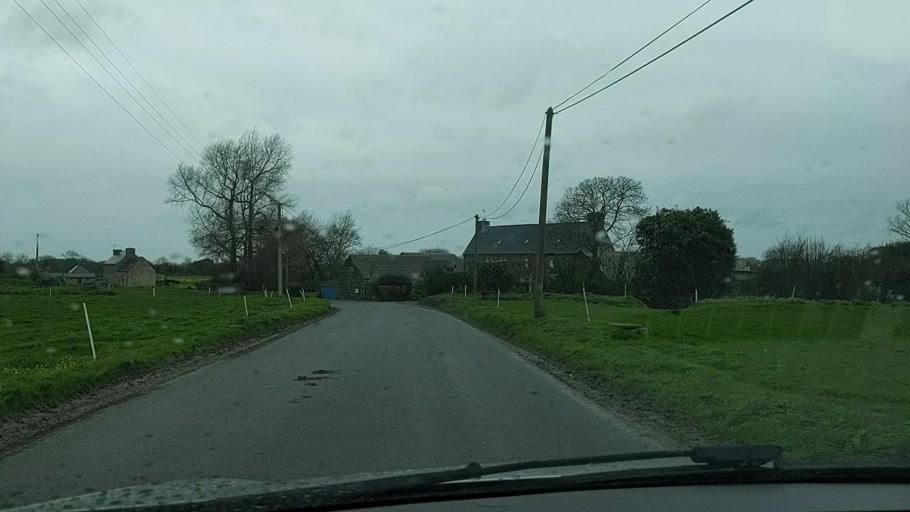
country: FR
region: Brittany
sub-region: Departement des Cotes-d'Armor
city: Pleumeur-Gautier
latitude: 48.8061
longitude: -3.1633
